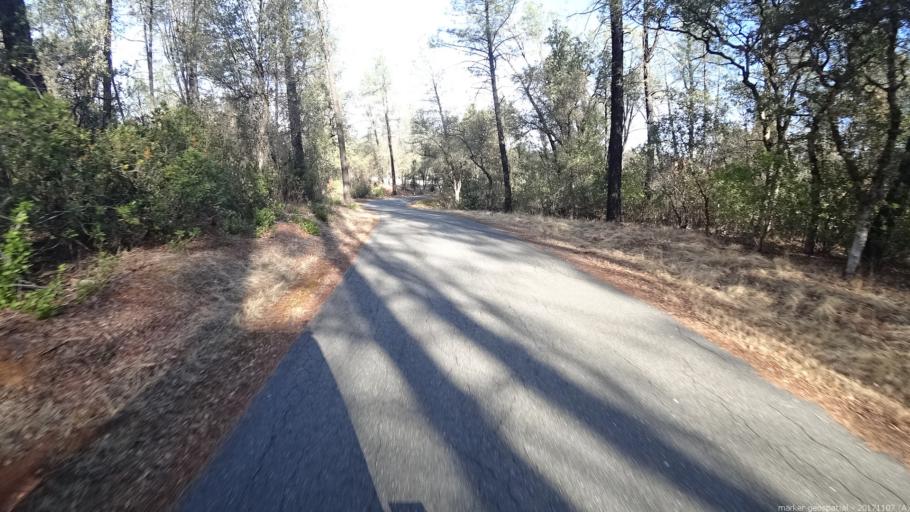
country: US
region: California
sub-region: Shasta County
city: Redding
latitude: 40.5508
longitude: -122.4471
